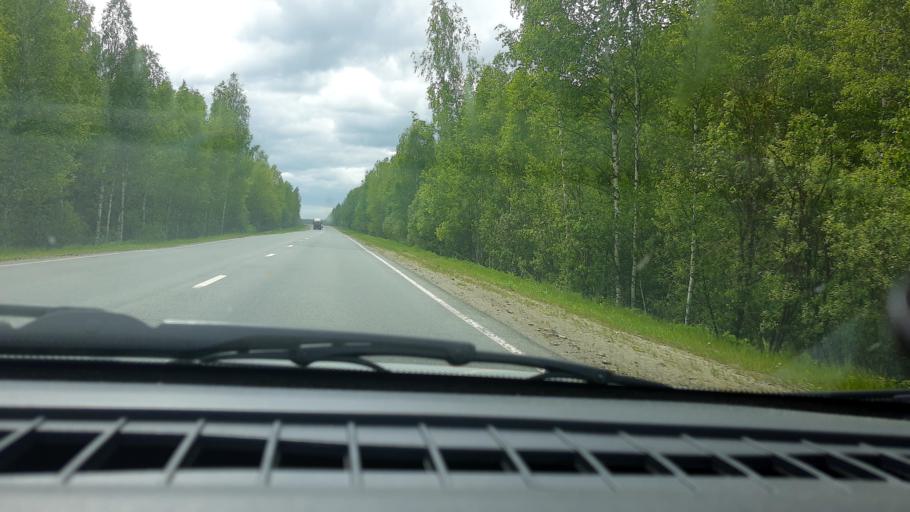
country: RU
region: Nizjnij Novgorod
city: Semenov
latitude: 56.7813
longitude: 44.4345
